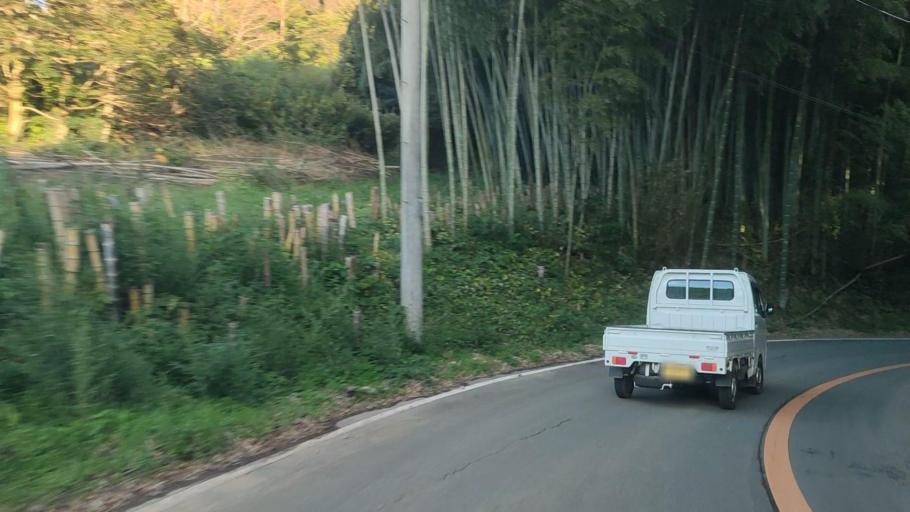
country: JP
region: Shizuoka
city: Mishima
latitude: 35.1343
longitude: 138.9674
